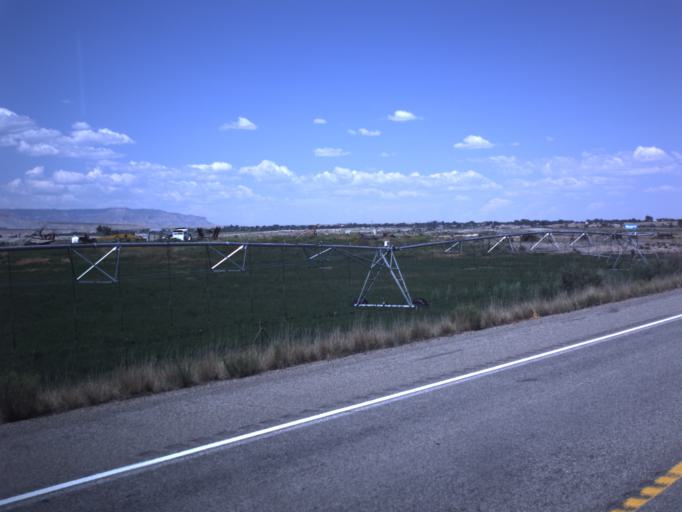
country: US
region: Utah
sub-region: Emery County
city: Castle Dale
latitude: 39.1854
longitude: -111.0329
